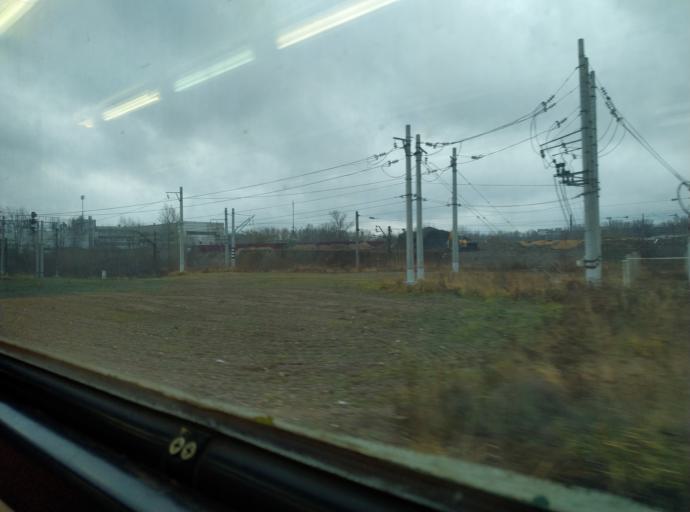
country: RU
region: Moscow
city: Nekrasovka
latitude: 55.6729
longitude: 37.9221
